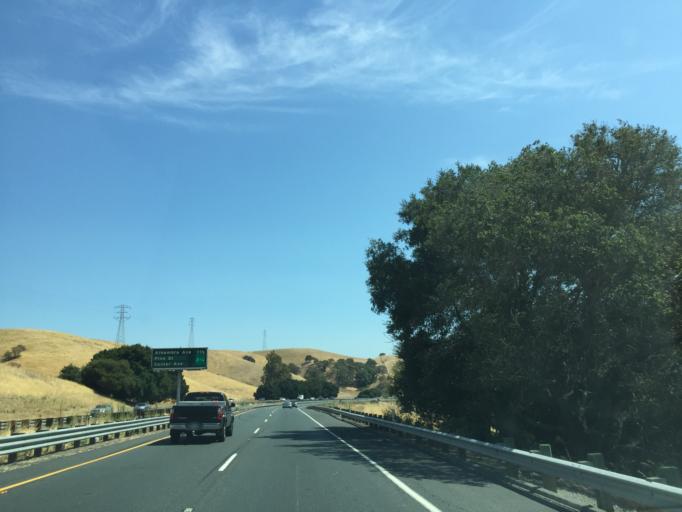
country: US
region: California
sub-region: Contra Costa County
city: Martinez
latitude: 38.0016
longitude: -122.1503
